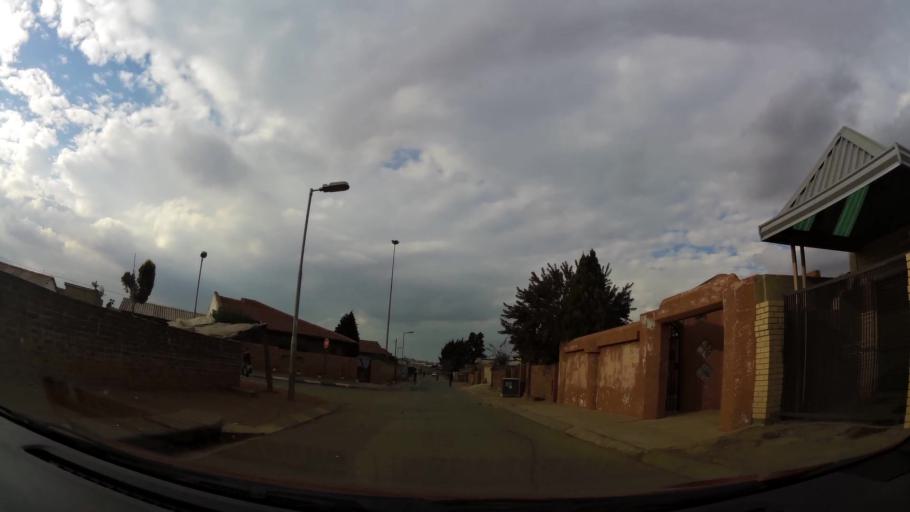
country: ZA
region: Gauteng
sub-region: City of Johannesburg Metropolitan Municipality
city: Soweto
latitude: -26.2524
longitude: 27.8304
